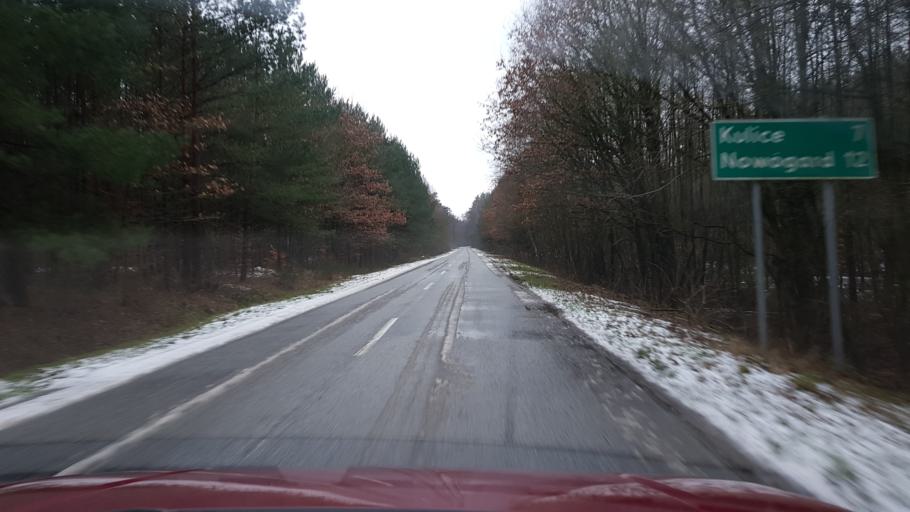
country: PL
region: West Pomeranian Voivodeship
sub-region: Powiat gryficki
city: Ploty
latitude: 53.6972
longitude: 15.2683
